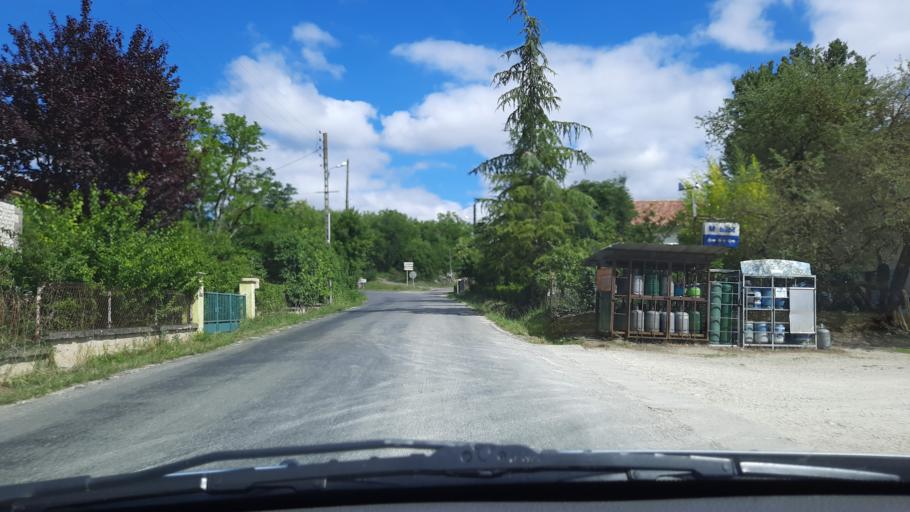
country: FR
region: Midi-Pyrenees
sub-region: Departement du Lot
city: Castelnau-Montratier
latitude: 44.2946
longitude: 1.4527
